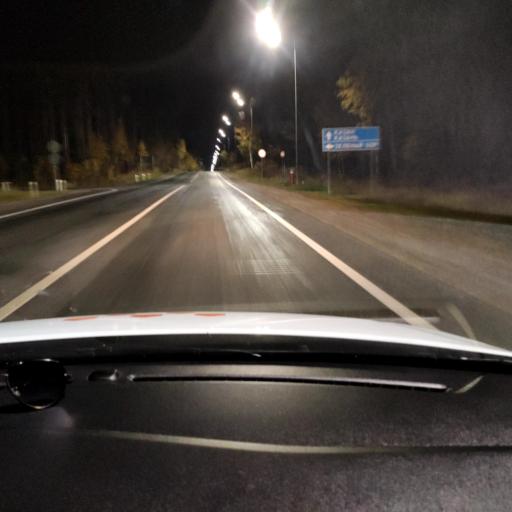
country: RU
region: Tatarstan
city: Verkhniy Uslon
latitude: 55.6395
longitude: 49.0290
